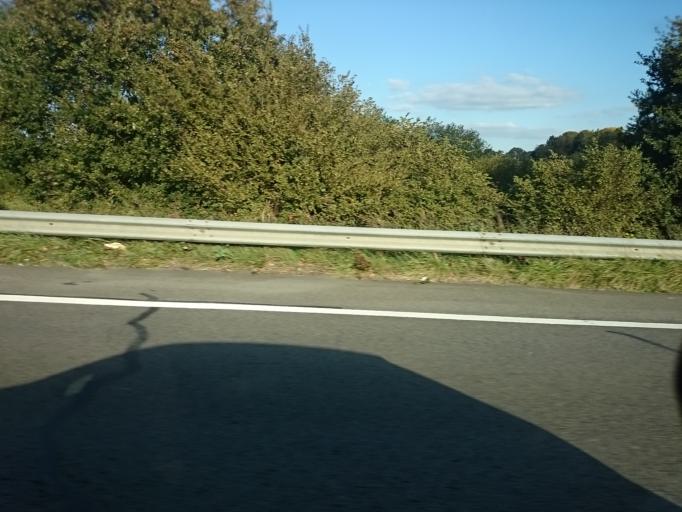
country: FR
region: Pays de la Loire
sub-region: Departement de la Loire-Atlantique
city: Treillieres
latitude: 47.3324
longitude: -1.6516
